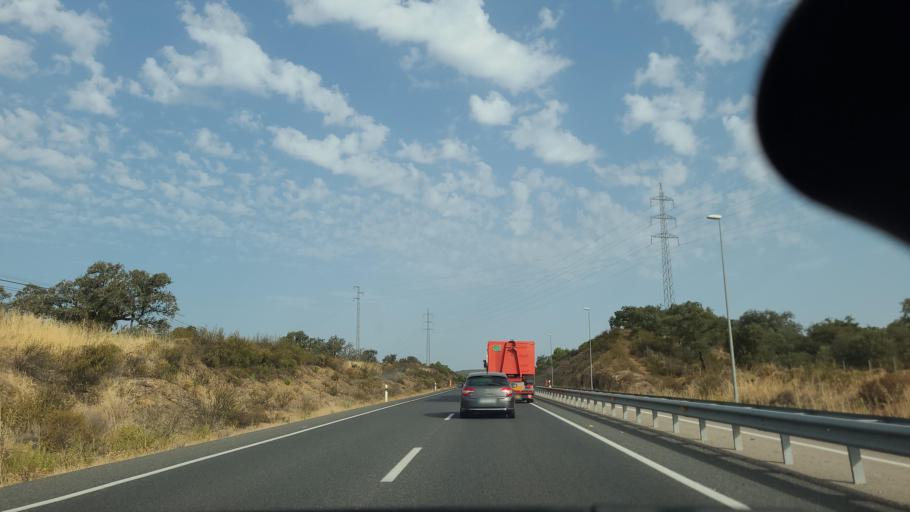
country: ES
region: Andalusia
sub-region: Province of Cordoba
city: Villaharta
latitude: 38.0877
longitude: -4.8607
